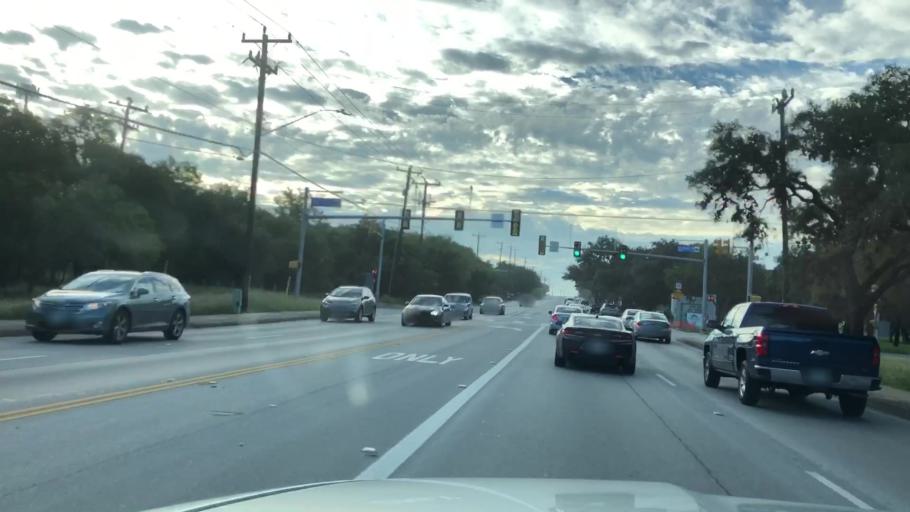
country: US
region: Texas
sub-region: Bexar County
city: Leon Valley
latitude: 29.5343
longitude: -98.6067
